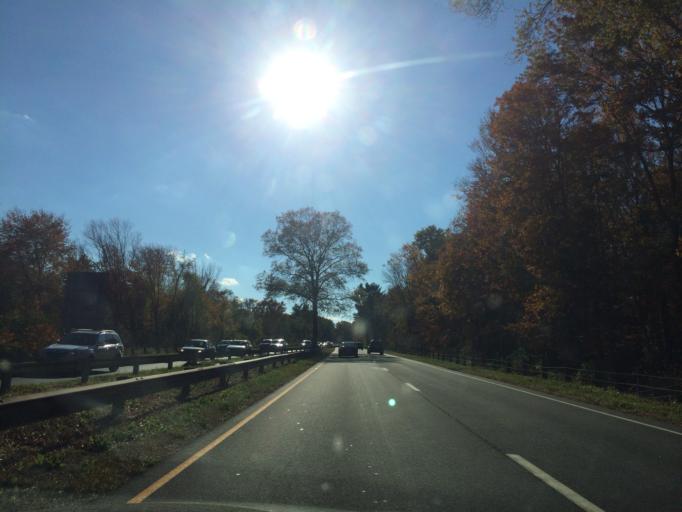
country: US
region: Connecticut
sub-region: Fairfield County
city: Westport
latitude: 41.1602
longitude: -73.3919
